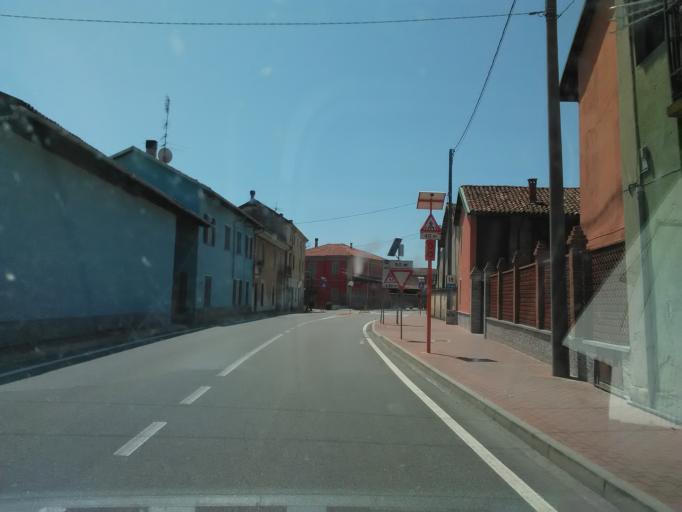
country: IT
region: Piedmont
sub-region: Provincia di Vercelli
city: Greggio
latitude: 45.4518
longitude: 8.3853
